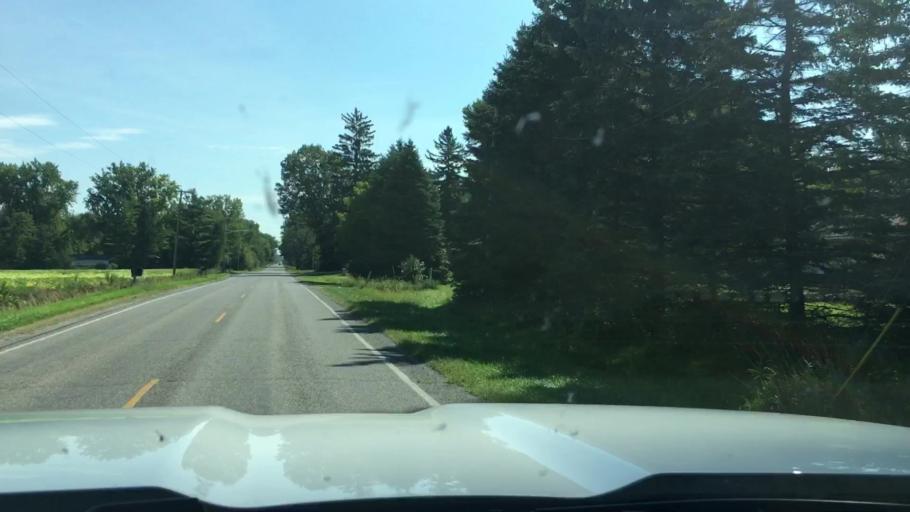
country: US
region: Michigan
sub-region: Saginaw County
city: Freeland
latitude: 43.5252
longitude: -84.1523
